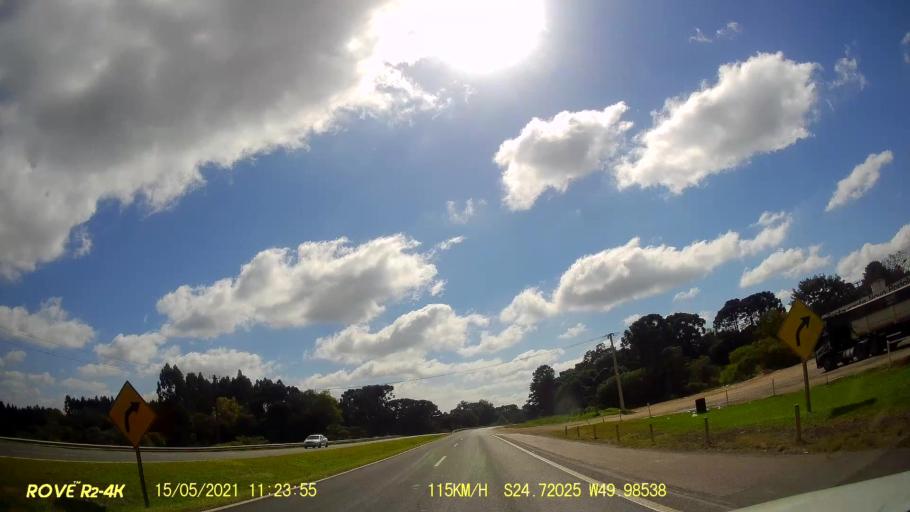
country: BR
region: Parana
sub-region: Castro
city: Castro
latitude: -24.7205
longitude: -49.9851
